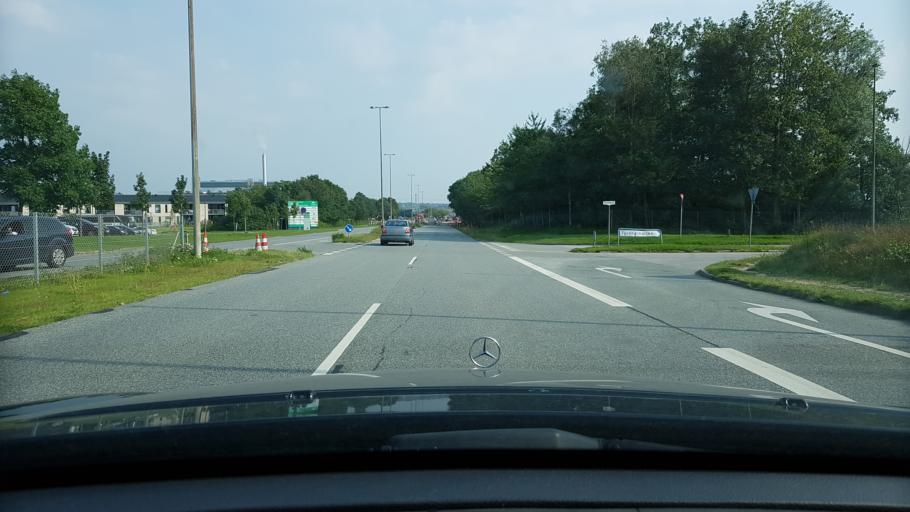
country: DK
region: North Denmark
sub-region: Alborg Kommune
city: Gistrup
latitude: 57.0263
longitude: 10.0024
